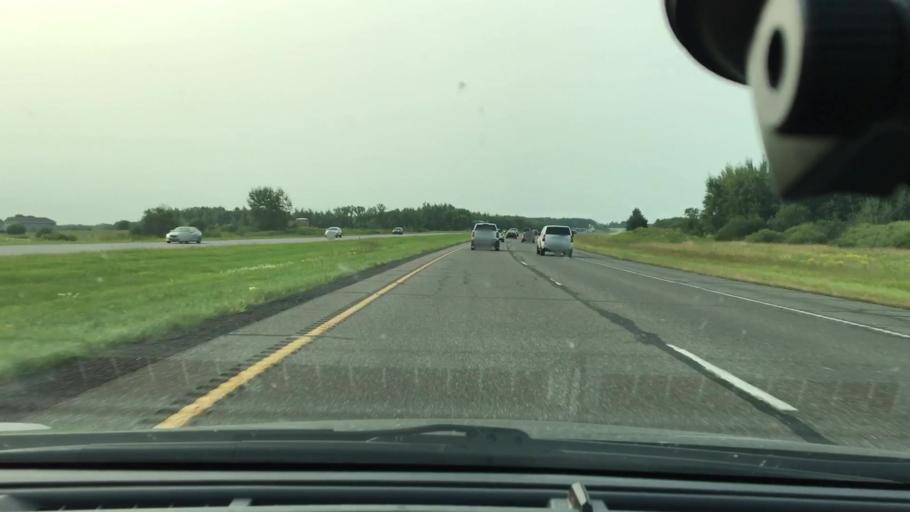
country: US
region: Minnesota
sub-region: Mille Lacs County
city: Milaca
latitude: 45.7676
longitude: -93.6436
